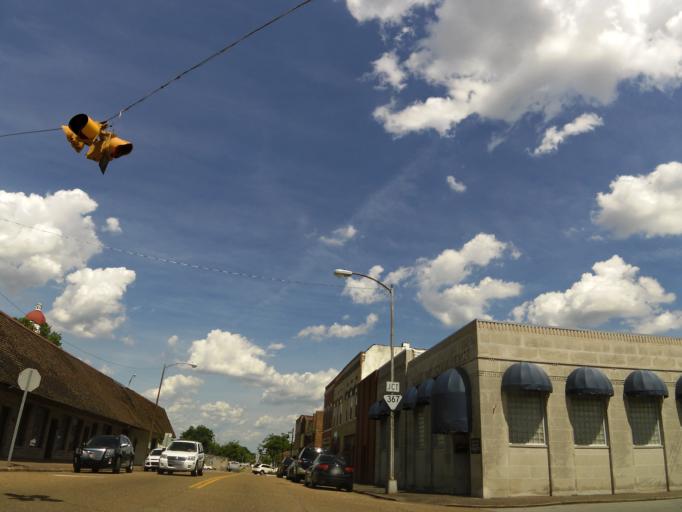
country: US
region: Tennessee
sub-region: Gibson County
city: Trenton
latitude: 35.9807
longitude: -88.9429
